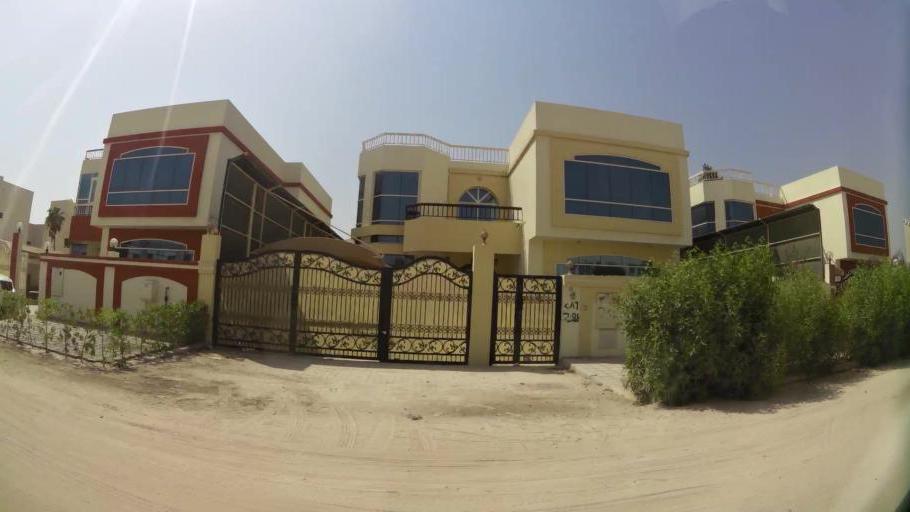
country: AE
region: Ajman
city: Ajman
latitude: 25.3908
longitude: 55.4218
